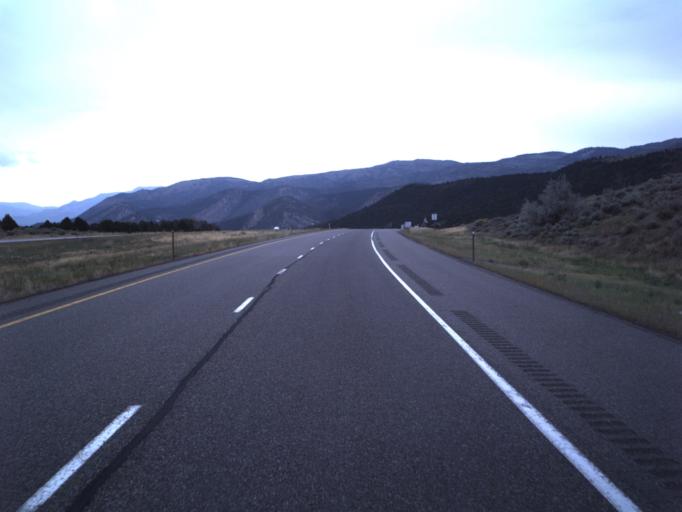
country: US
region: Utah
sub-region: Sevier County
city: Monroe
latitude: 38.5533
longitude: -112.4127
